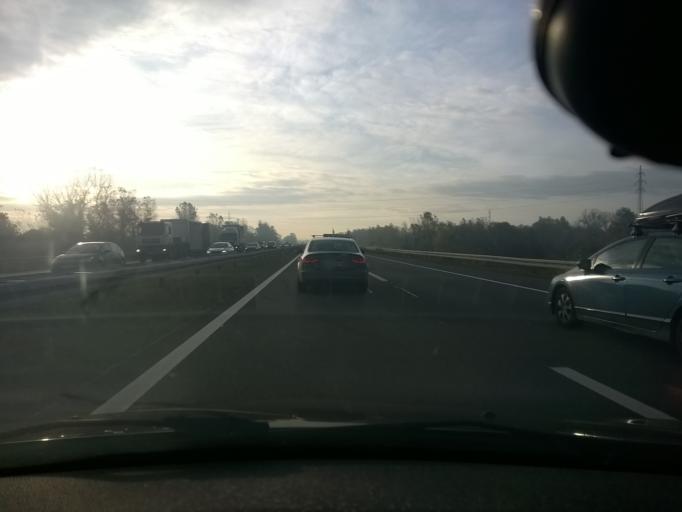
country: HR
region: Zagrebacka
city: Bestovje
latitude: 45.8071
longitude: 15.8335
